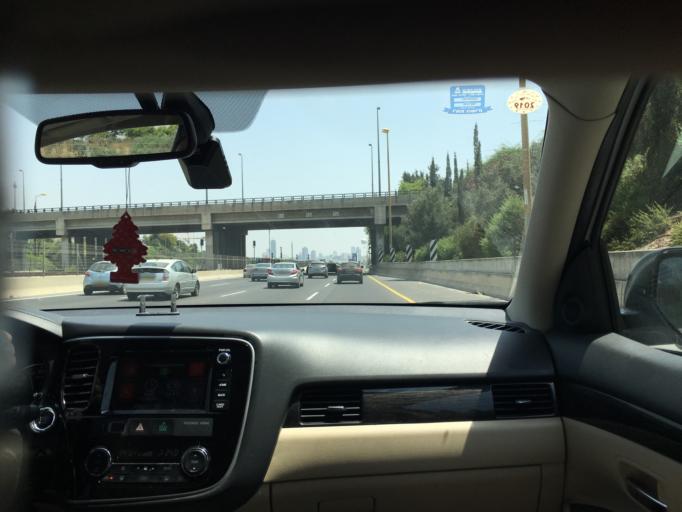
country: IL
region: Tel Aviv
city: Ramat Gan
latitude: 32.1200
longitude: 34.8100
